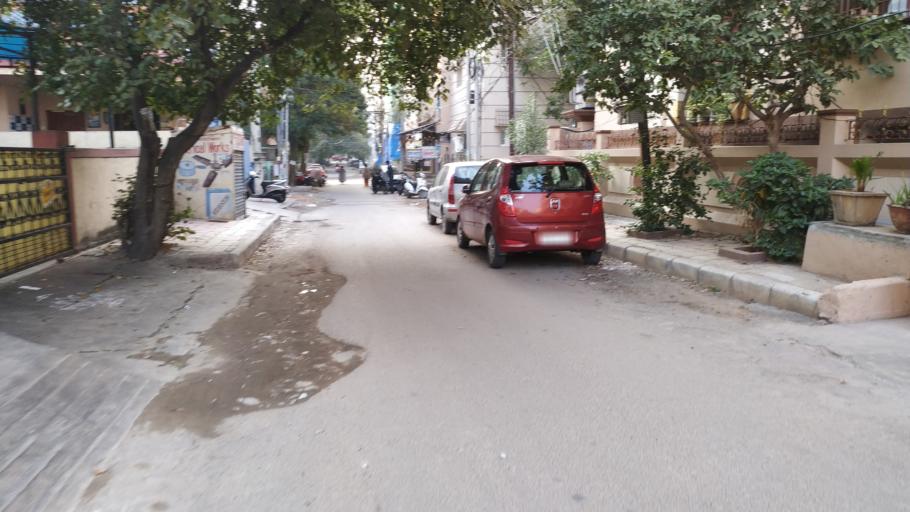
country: IN
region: Telangana
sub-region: Rangareddi
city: Kukatpalli
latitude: 17.4431
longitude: 78.4477
